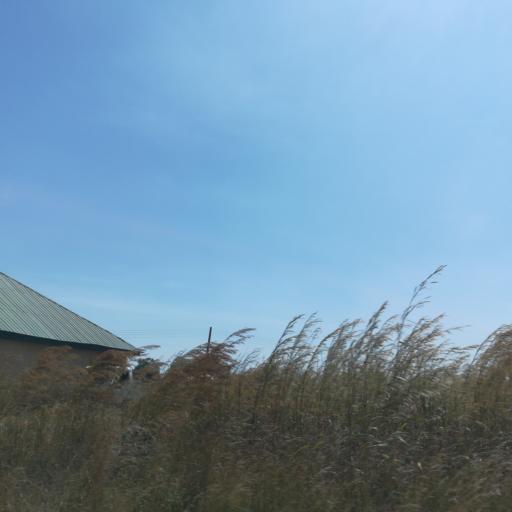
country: NG
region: Plateau
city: Bukuru
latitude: 9.7810
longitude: 8.9066
